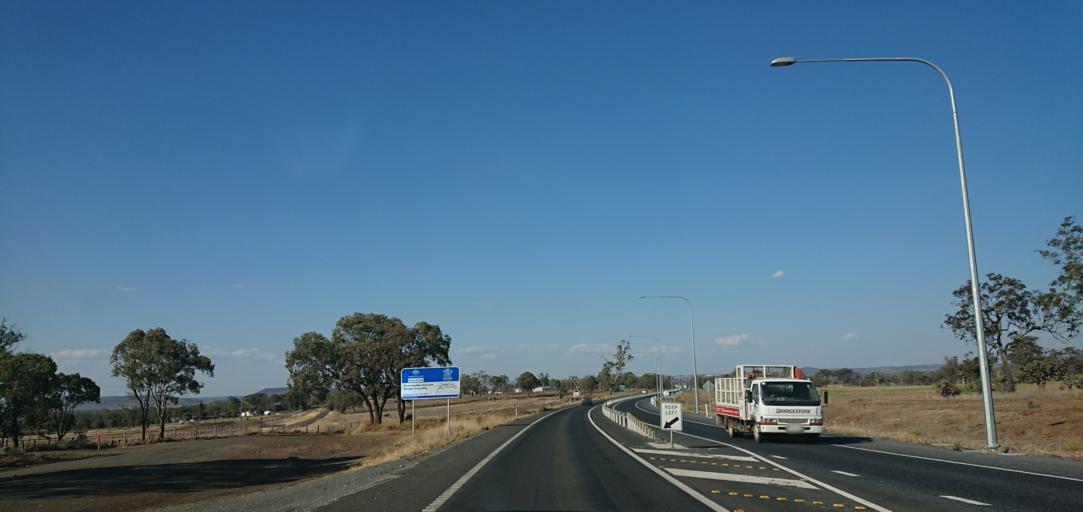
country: AU
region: Queensland
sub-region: Toowoomba
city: Westbrook
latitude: -27.6201
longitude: 151.7678
